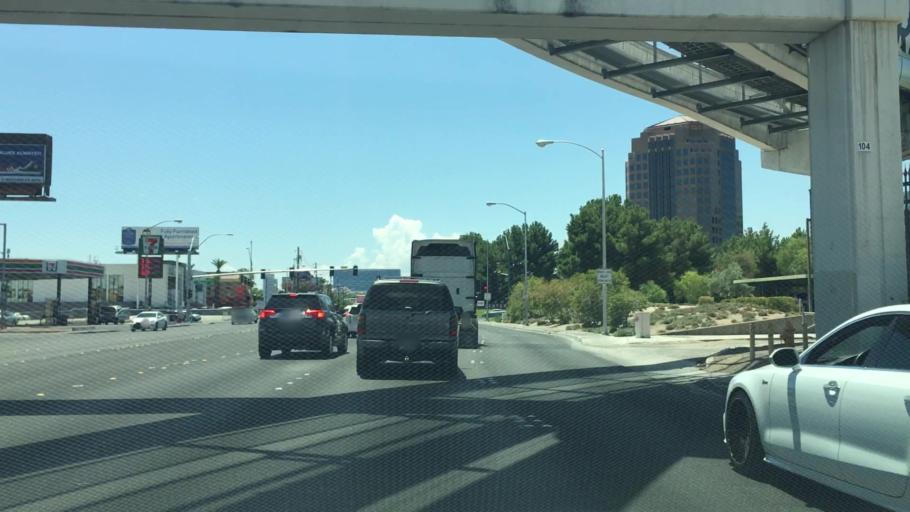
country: US
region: Nevada
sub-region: Clark County
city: Paradise
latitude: 36.1224
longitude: -115.1550
